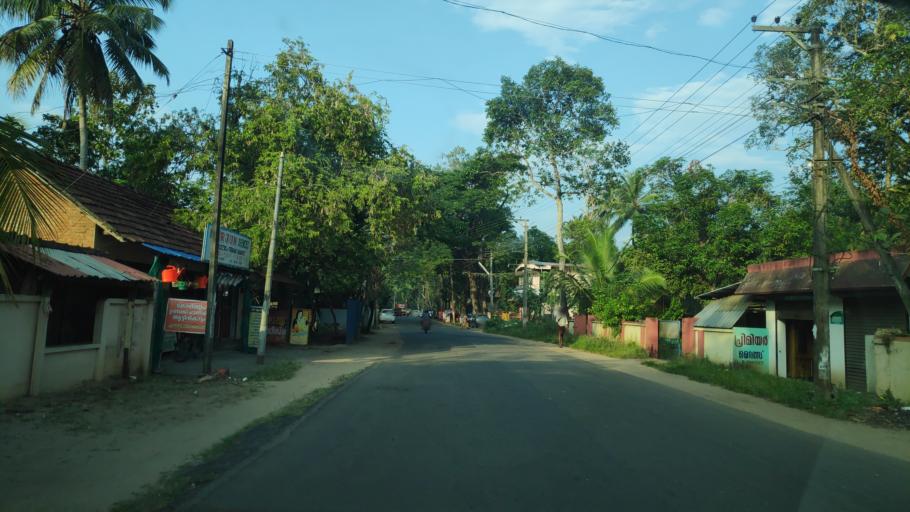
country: IN
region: Kerala
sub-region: Alappuzha
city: Shertallai
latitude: 9.6081
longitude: 76.3609
